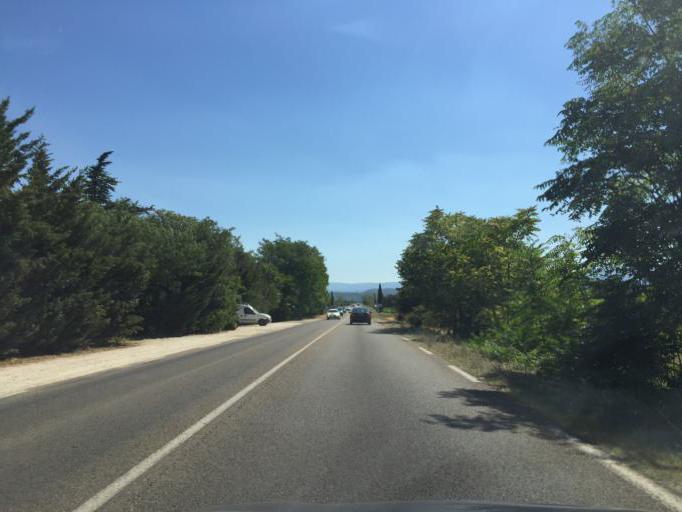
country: FR
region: Provence-Alpes-Cote d'Azur
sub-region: Departement du Vaucluse
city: Maubec
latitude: 43.8651
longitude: 5.1630
